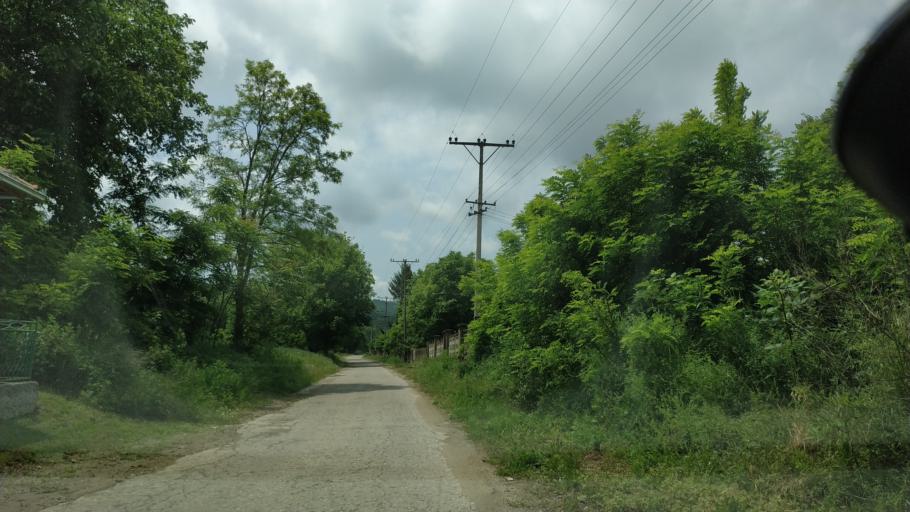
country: RS
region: Central Serbia
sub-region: Nisavski Okrug
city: Aleksinac
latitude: 43.4239
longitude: 21.7071
